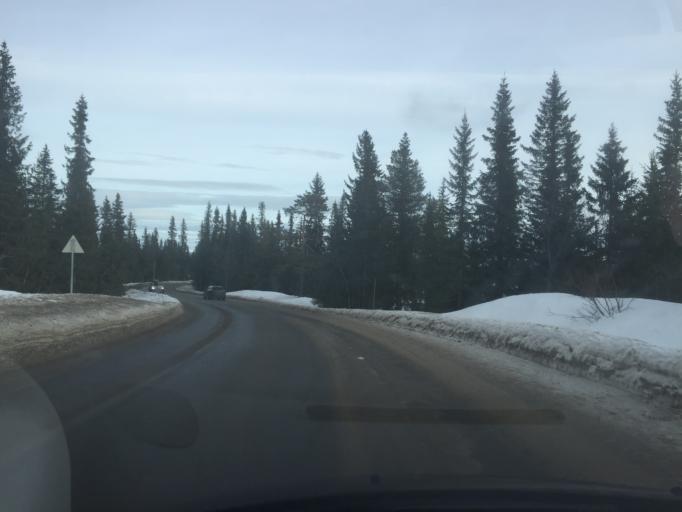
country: NO
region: Hedmark
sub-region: Trysil
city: Innbygda
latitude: 61.3343
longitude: 12.1724
